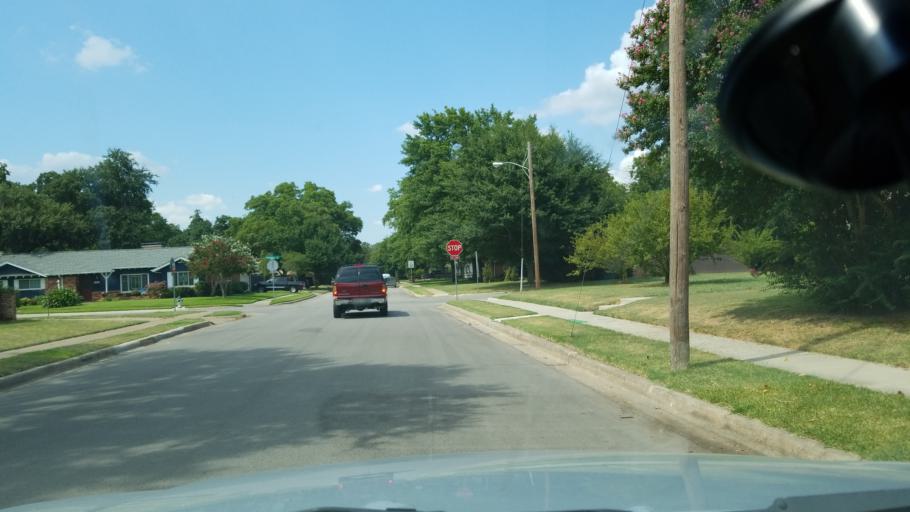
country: US
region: Texas
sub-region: Dallas County
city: Irving
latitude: 32.8180
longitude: -96.9794
